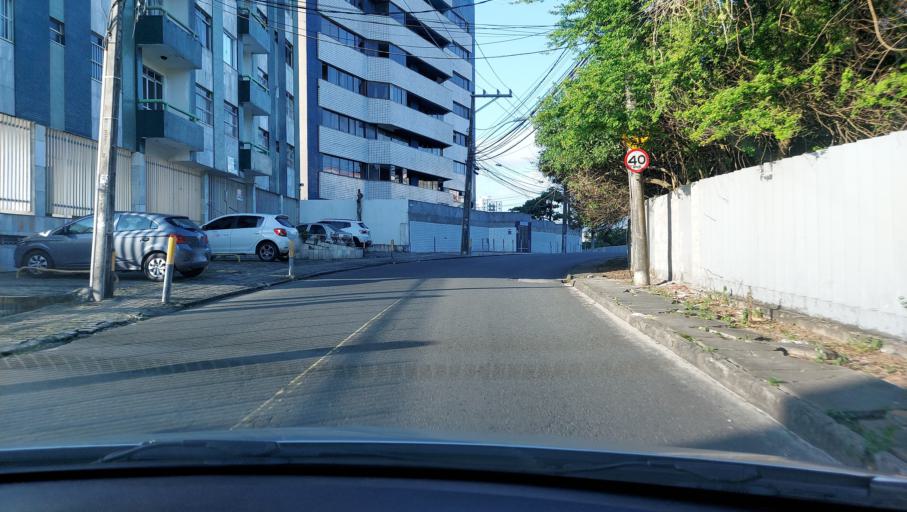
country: BR
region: Bahia
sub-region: Salvador
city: Salvador
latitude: -12.9853
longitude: -38.4429
